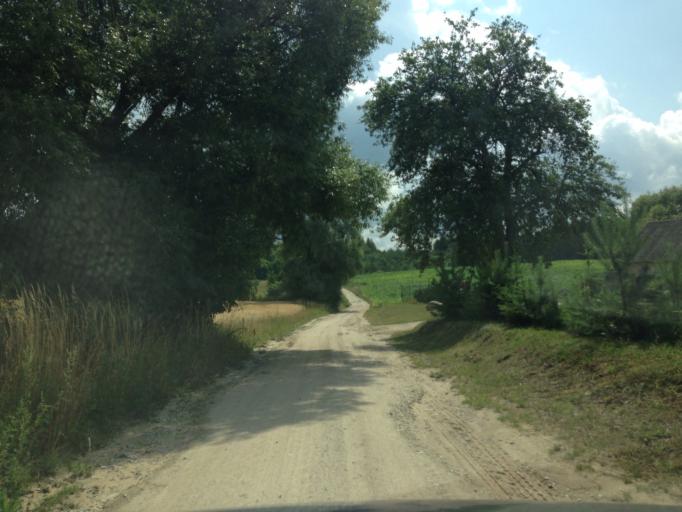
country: PL
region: Kujawsko-Pomorskie
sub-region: Powiat brodnicki
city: Gorzno
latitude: 53.2258
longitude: 19.6464
